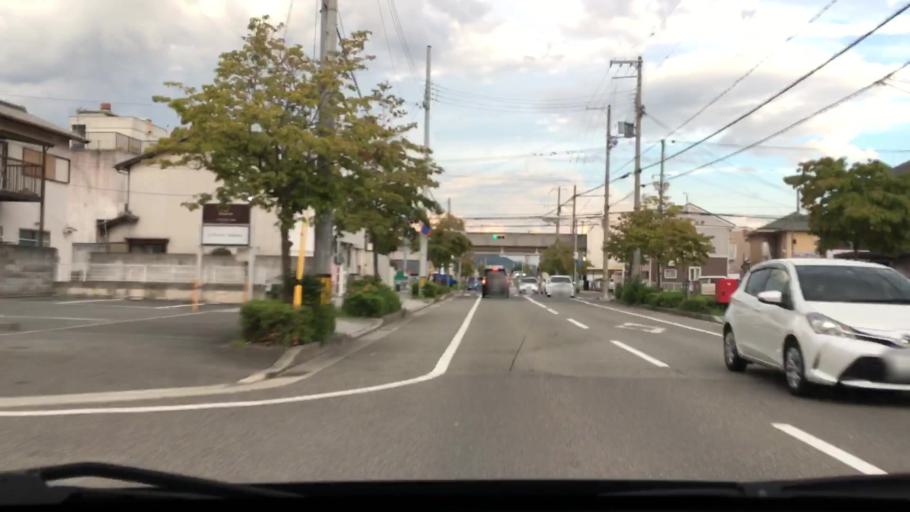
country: JP
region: Hyogo
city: Himeji
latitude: 34.8502
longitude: 134.7051
